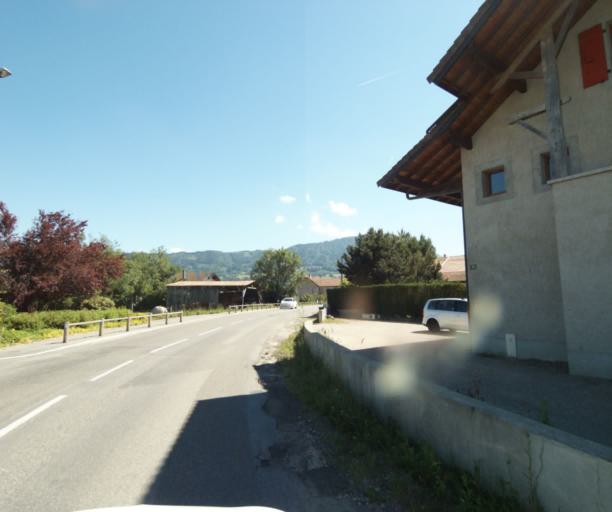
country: FR
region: Rhone-Alpes
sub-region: Departement de la Haute-Savoie
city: Bons-en-Chablais
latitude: 46.2754
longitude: 6.3615
